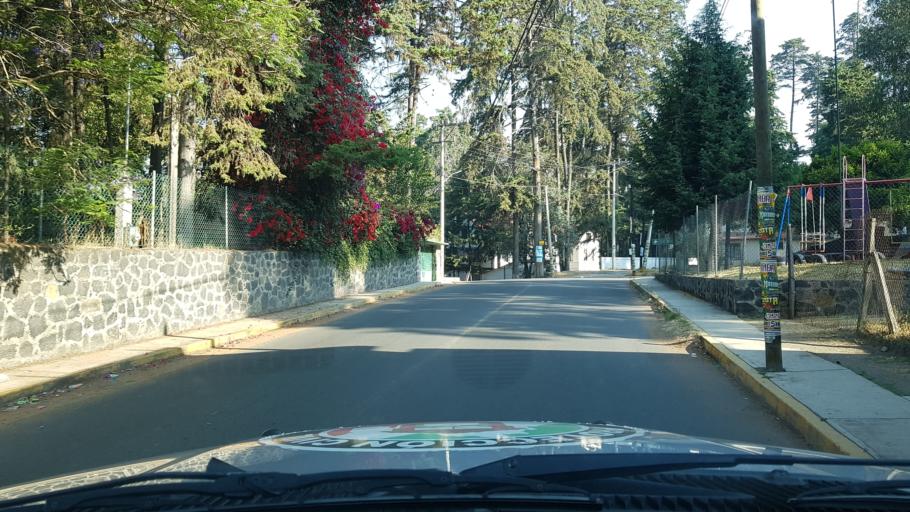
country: MX
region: Mexico
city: Ozumba de Alzate
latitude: 19.0606
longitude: -98.7799
